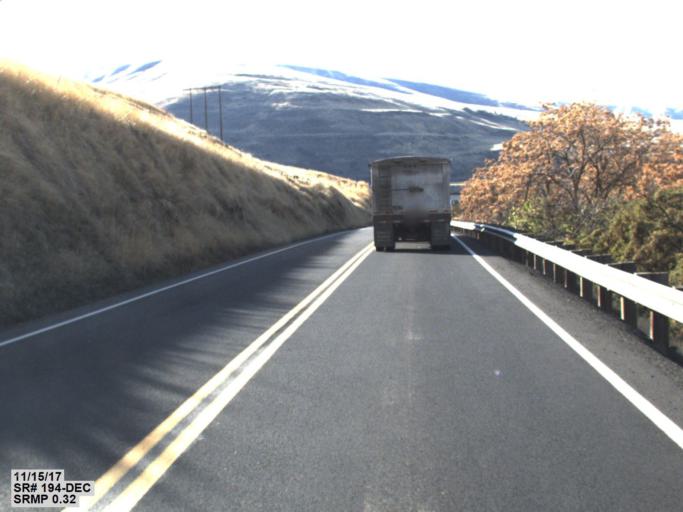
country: US
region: Washington
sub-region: Whitman County
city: Colfax
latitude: 46.7068
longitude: -117.4661
